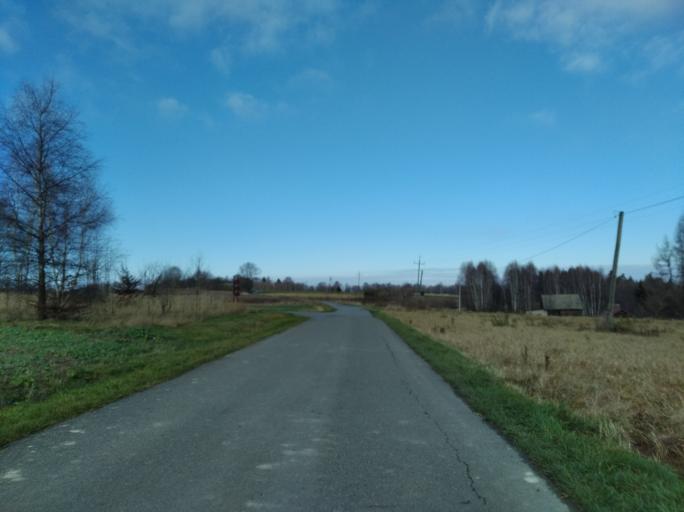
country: PL
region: Subcarpathian Voivodeship
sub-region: Powiat strzyzowski
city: Babica
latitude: 49.9114
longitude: 21.8484
